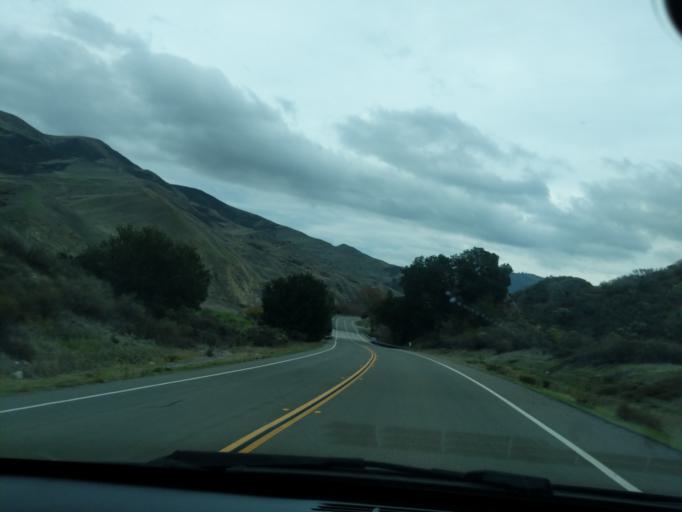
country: US
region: California
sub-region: Monterey County
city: Soledad
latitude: 36.6143
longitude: -121.2135
